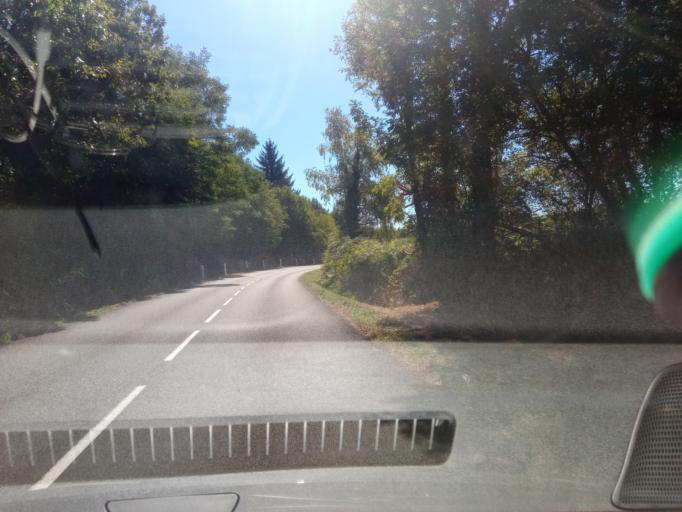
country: FR
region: Limousin
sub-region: Departement de la Haute-Vienne
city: Nantiat
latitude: 46.0728
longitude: 1.2032
